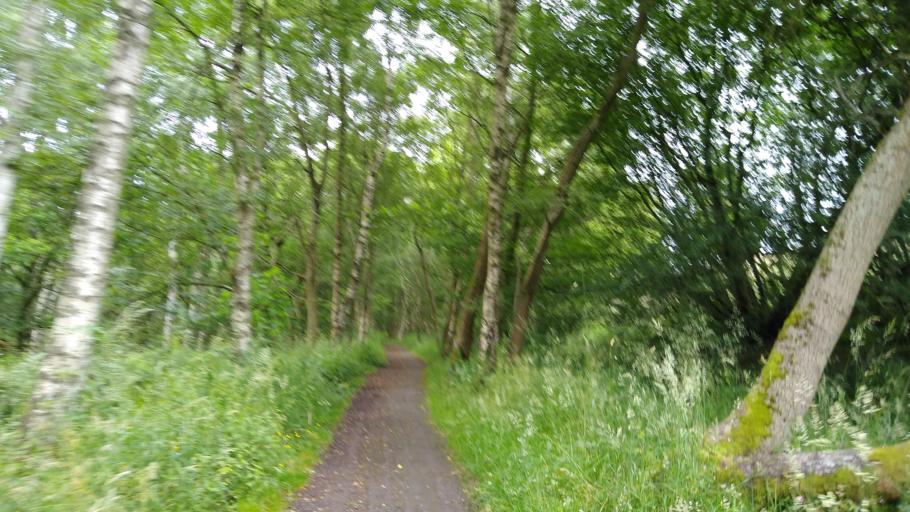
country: GB
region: England
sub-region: Northumberland
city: Greenhead
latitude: 54.9452
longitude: -2.4917
